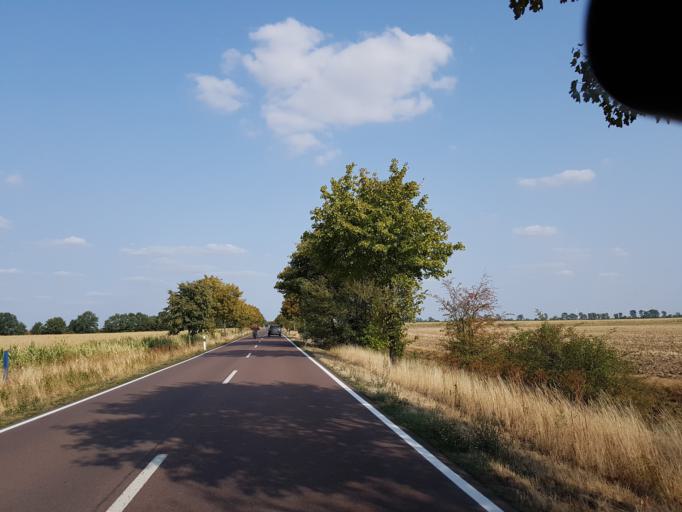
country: DE
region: Saxony-Anhalt
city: Kemberg
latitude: 51.8064
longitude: 12.6579
